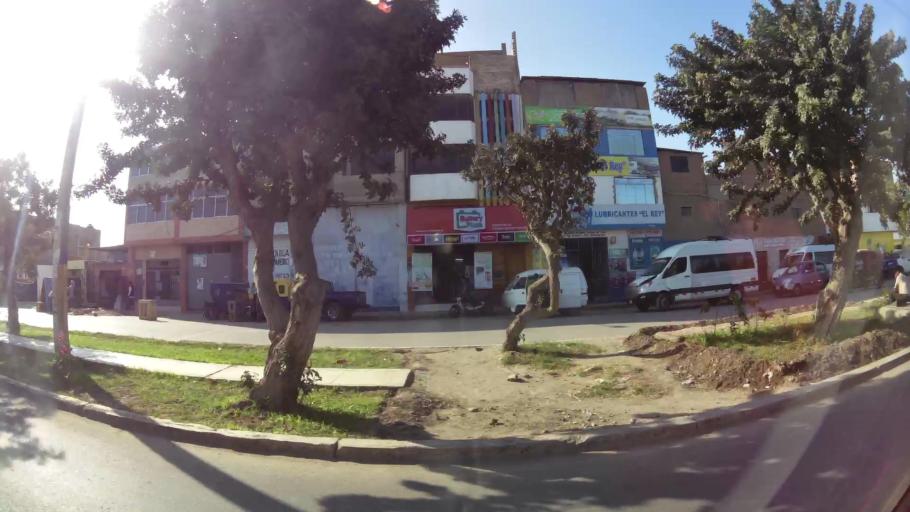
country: PE
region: Lambayeque
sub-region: Provincia de Chiclayo
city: Chiclayo
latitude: -6.7626
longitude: -79.8461
